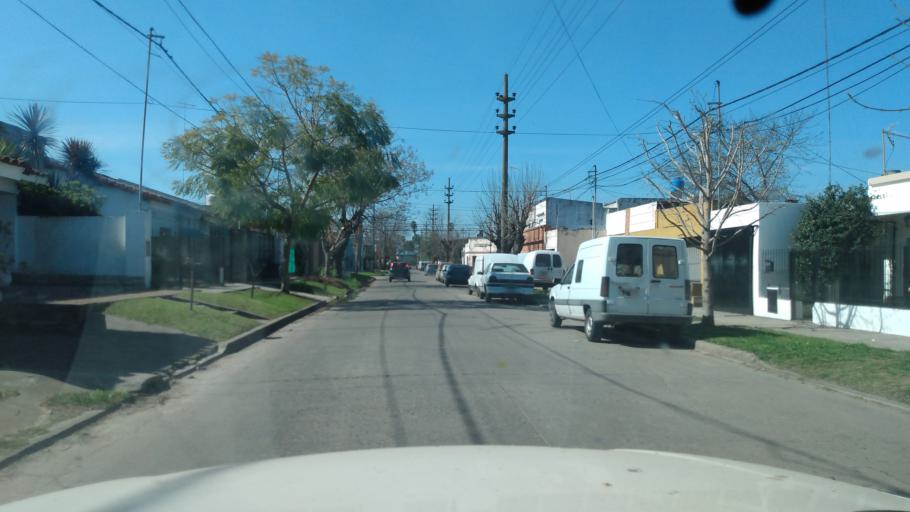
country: AR
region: Buenos Aires
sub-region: Partido de Lujan
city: Lujan
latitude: -34.5816
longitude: -59.1055
